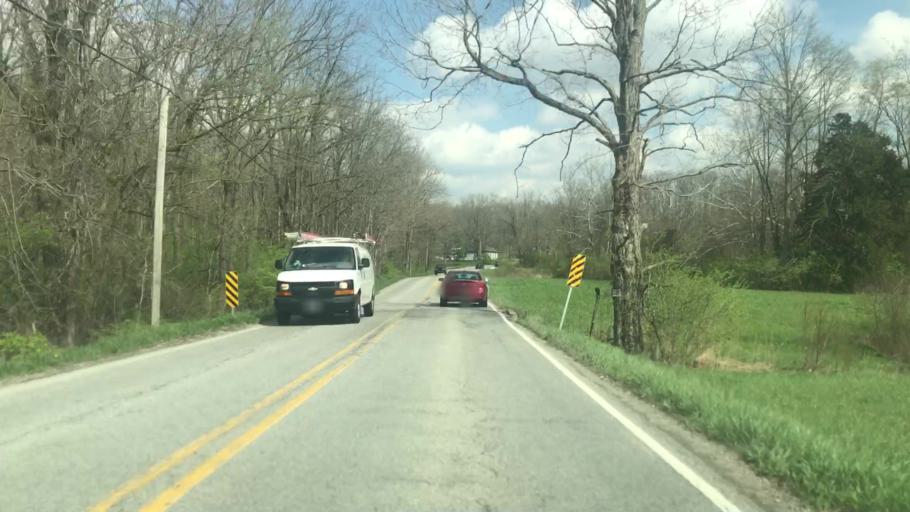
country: US
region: Indiana
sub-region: Johnson County
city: Waterloo
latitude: 39.5523
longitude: -86.2132
